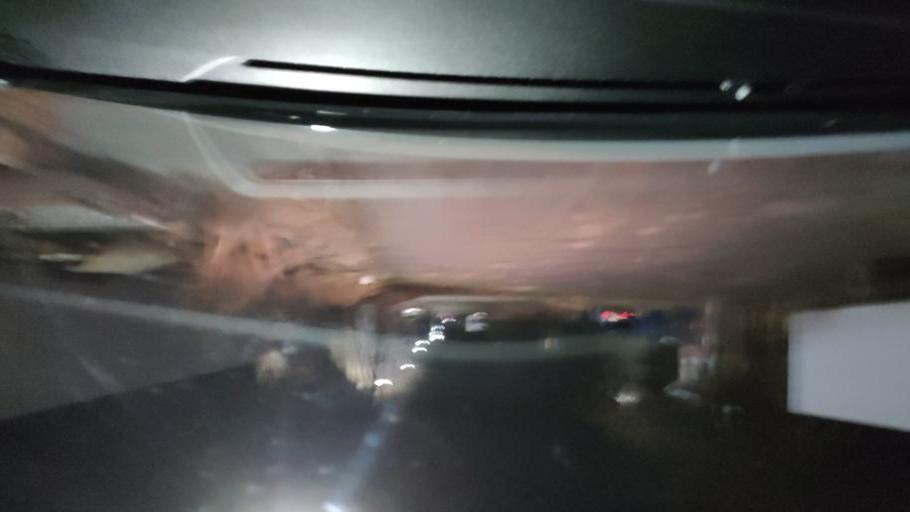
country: RU
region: Tatarstan
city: Vysokaya Gora
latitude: 55.8461
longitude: 49.2171
